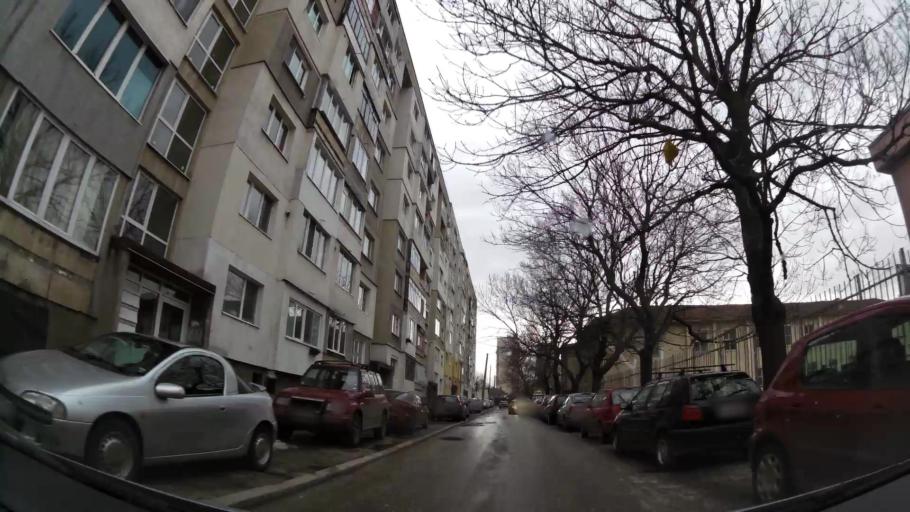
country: BG
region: Sofia-Capital
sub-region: Stolichna Obshtina
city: Sofia
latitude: 42.7256
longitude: 23.3010
